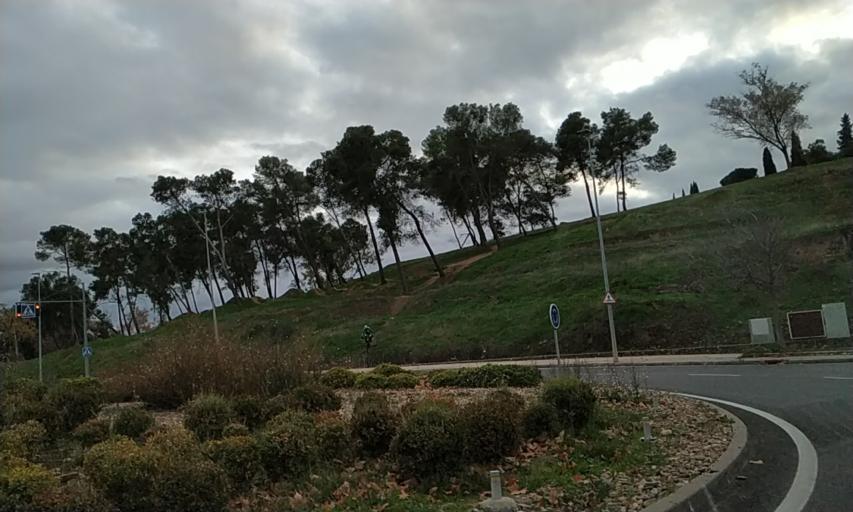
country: ES
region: Extremadura
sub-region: Provincia de Badajoz
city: Badajoz
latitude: 38.8827
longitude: -6.9647
